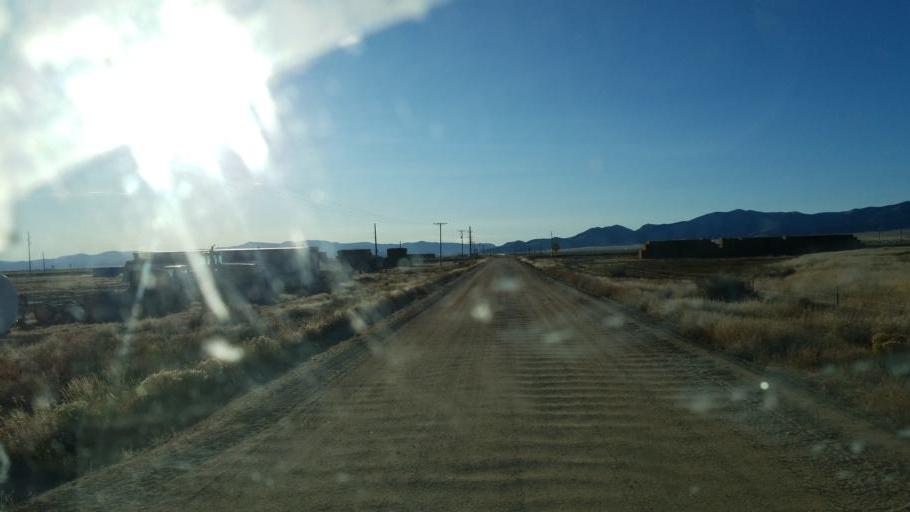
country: US
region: Colorado
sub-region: Saguache County
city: Saguache
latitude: 38.1005
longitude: -105.9162
